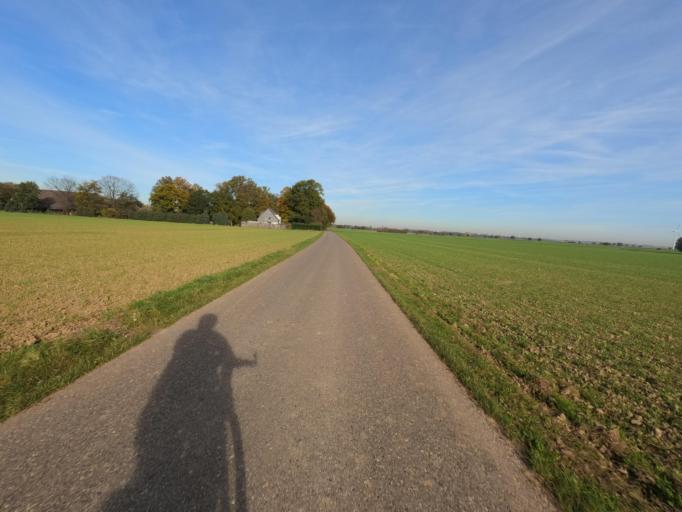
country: DE
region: North Rhine-Westphalia
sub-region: Regierungsbezirk Koln
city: Titz
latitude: 51.0586
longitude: 6.3843
